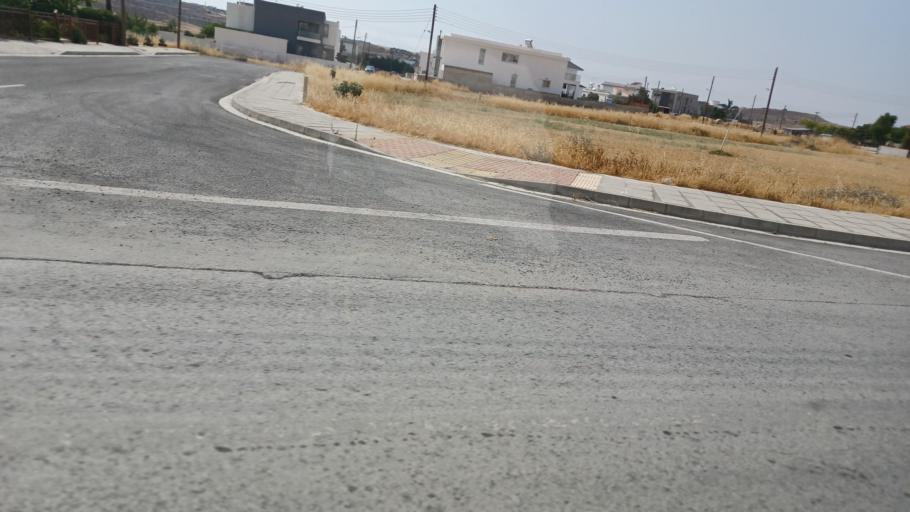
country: CY
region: Larnaka
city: Aradippou
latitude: 34.9308
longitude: 33.5431
